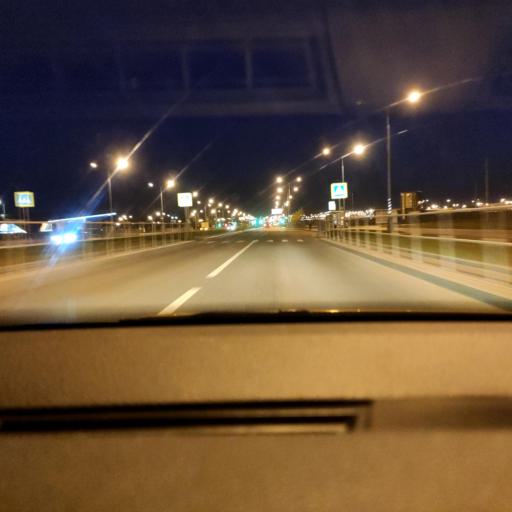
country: RU
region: Moskovskaya
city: Kommunarka
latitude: 55.5705
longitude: 37.4594
